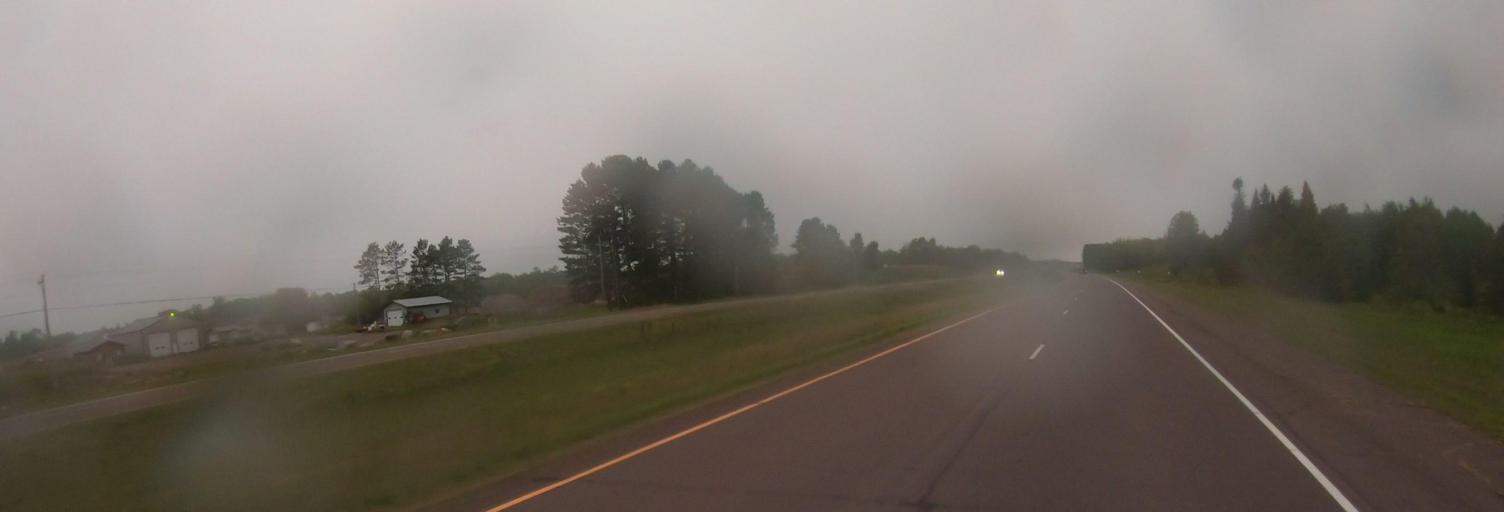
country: US
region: Minnesota
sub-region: Carlton County
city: Cloquet
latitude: 46.9108
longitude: -92.4700
